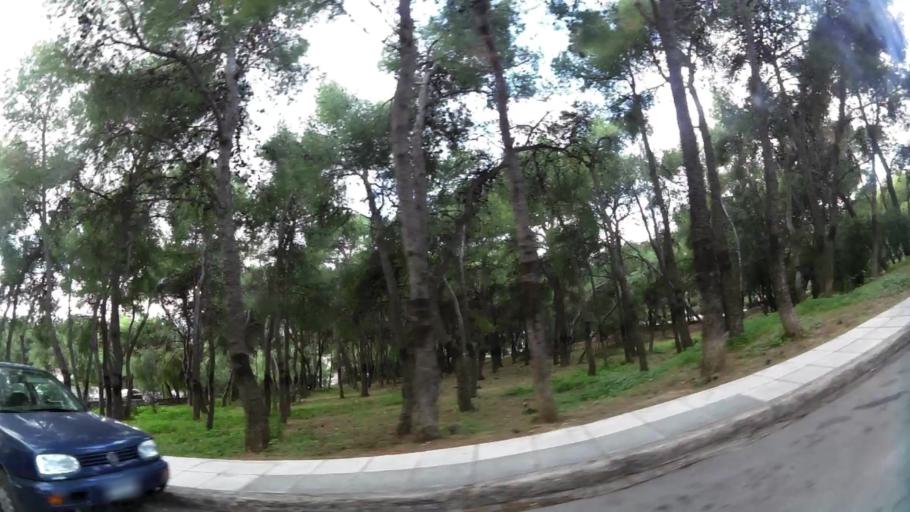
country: GR
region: Attica
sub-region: Nomarchia Athinas
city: Melissia
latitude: 38.0567
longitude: 23.8288
